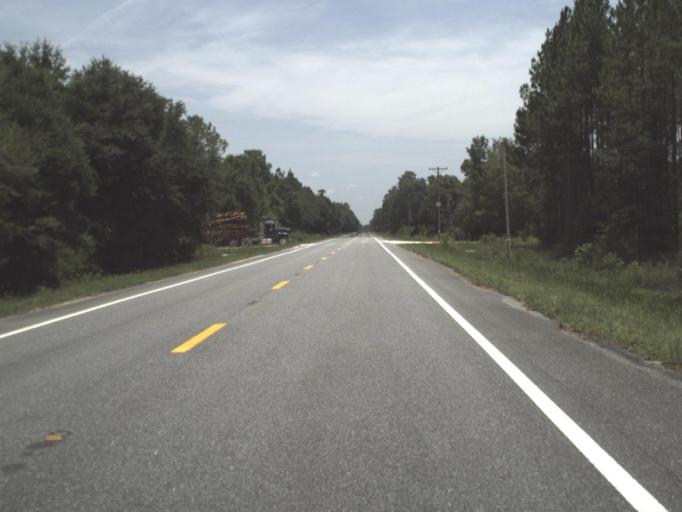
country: US
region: Florida
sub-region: Taylor County
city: Steinhatchee
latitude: 29.8297
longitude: -83.3141
